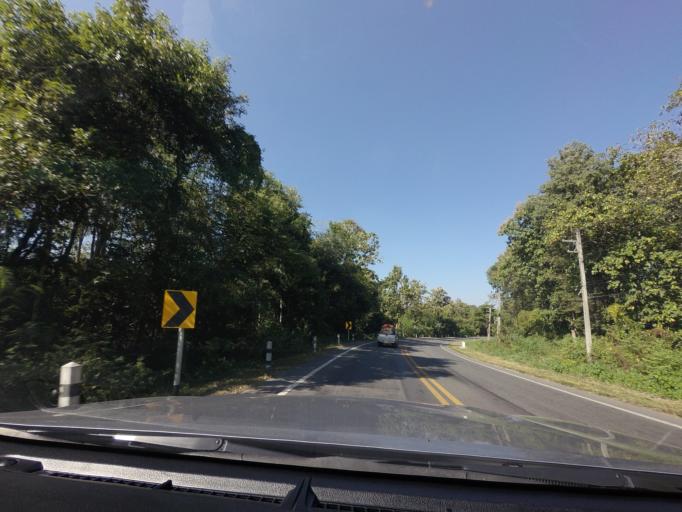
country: TH
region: Sukhothai
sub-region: Amphoe Si Satchanalai
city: Si Satchanalai
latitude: 17.6100
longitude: 99.7066
